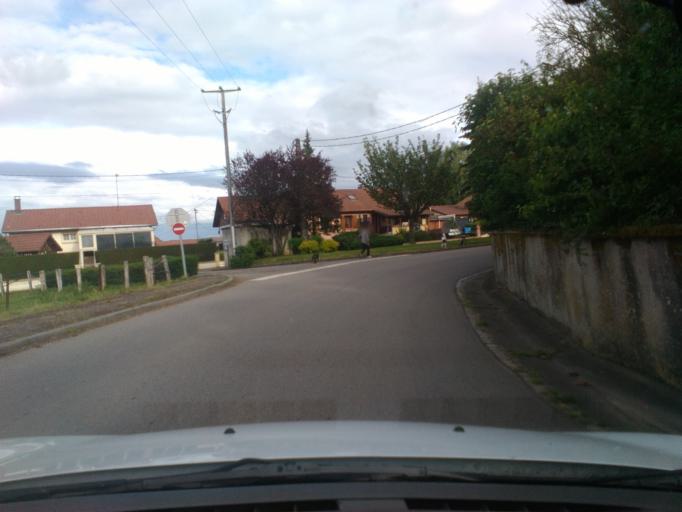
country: FR
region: Lorraine
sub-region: Departement des Vosges
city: Mirecourt
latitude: 48.3113
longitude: 6.0536
